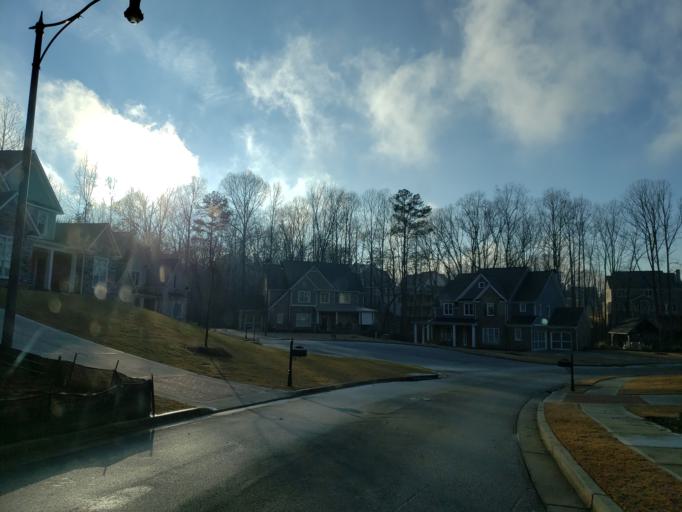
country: US
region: Georgia
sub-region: Cobb County
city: Kennesaw
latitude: 33.9836
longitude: -84.5919
